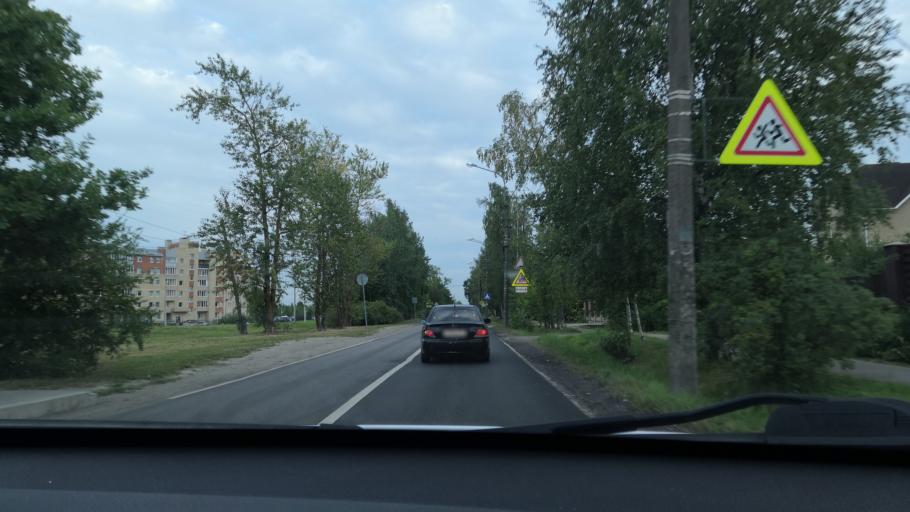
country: RU
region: St.-Petersburg
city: Pushkin
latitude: 59.6979
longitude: 30.4109
